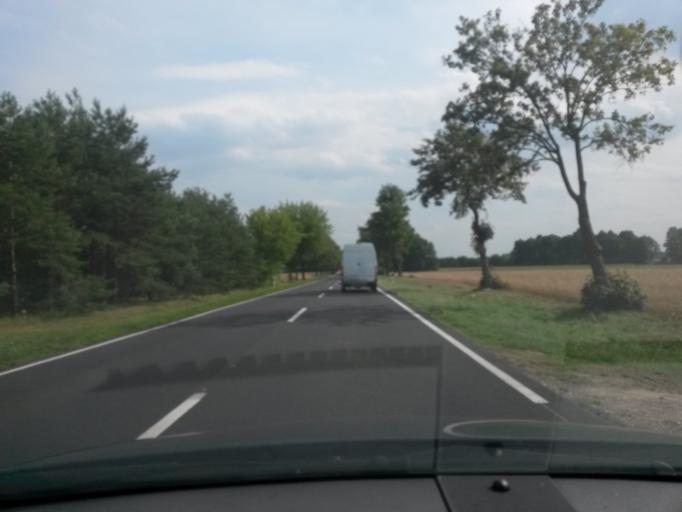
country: PL
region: Greater Poland Voivodeship
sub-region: Powiat sremski
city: Srem
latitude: 52.1399
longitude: 17.0394
